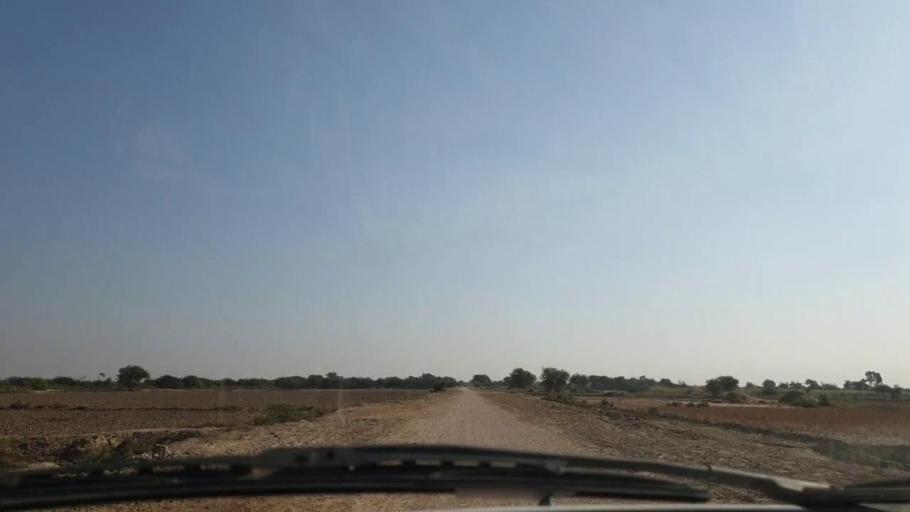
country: PK
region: Sindh
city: Bulri
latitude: 24.7986
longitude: 68.3940
